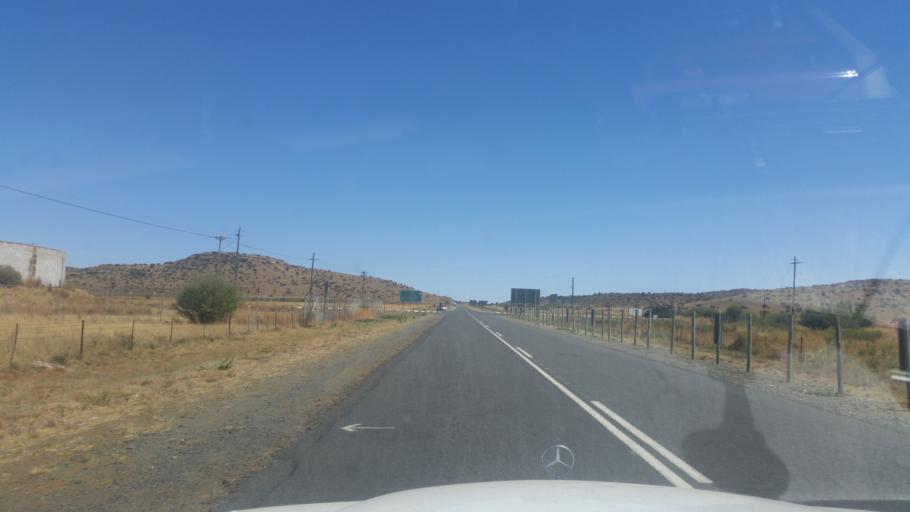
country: ZA
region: Eastern Cape
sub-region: Joe Gqabi District Municipality
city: Burgersdorp
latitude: -30.7795
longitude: 25.7613
